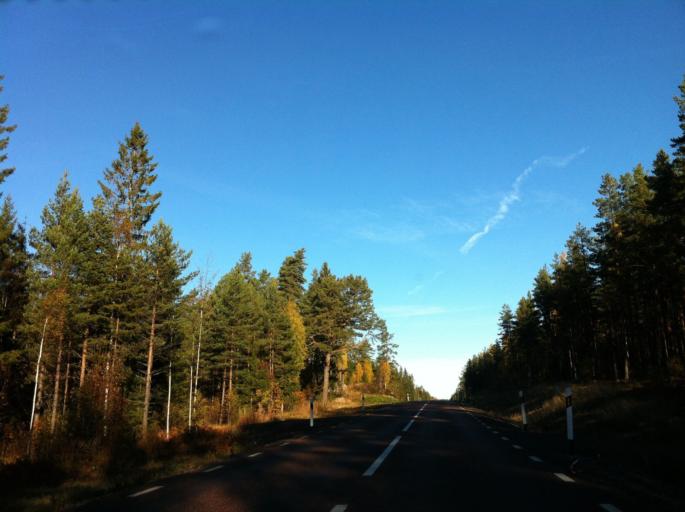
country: SE
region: Gaevleborg
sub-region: Gavle Kommun
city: Gavle
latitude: 60.5869
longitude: 17.1295
